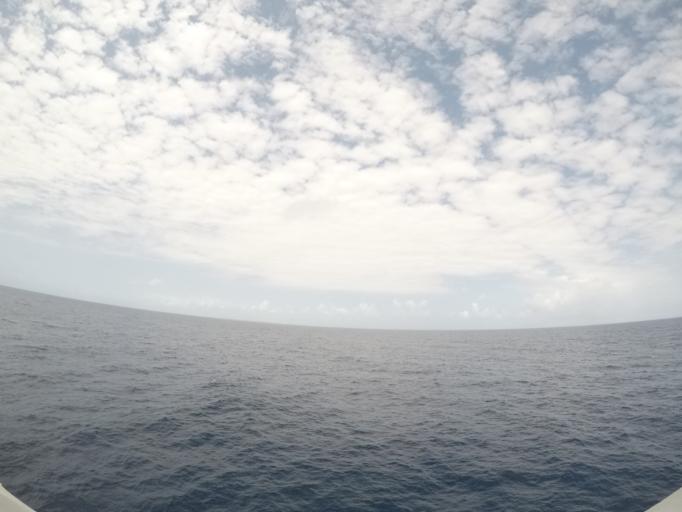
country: TZ
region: Zanzibar North
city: Nungwi
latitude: -5.5974
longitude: 39.3439
